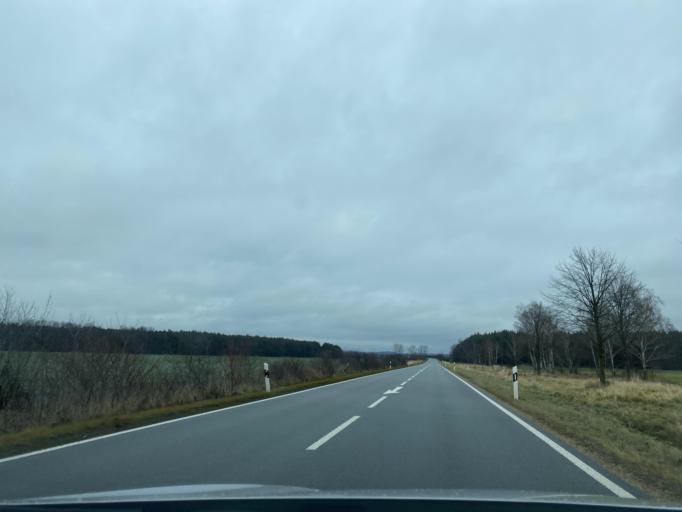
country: DE
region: Saxony
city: Goerlitz
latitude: 51.2266
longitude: 14.9631
